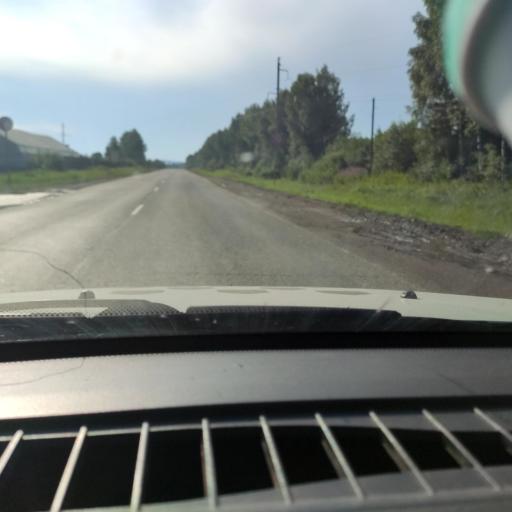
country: RU
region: Kirov
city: Kostino
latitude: 58.8591
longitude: 53.1784
